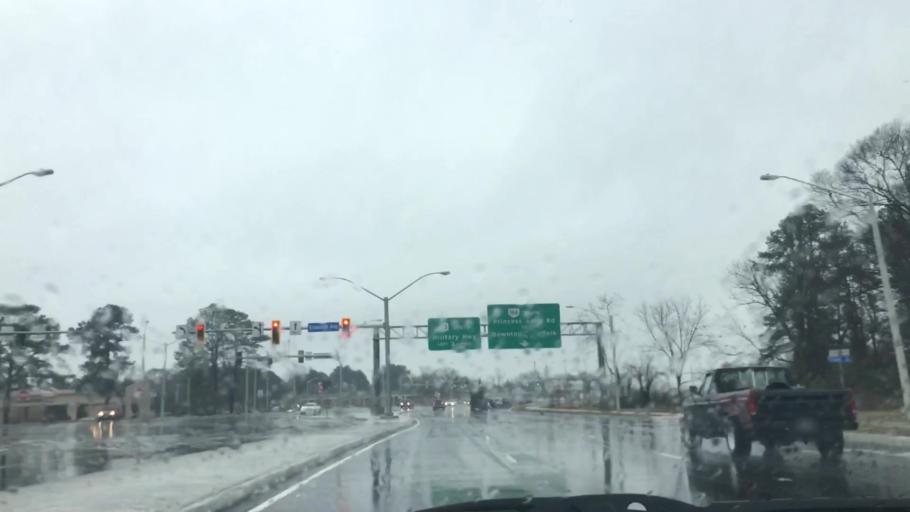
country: US
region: Virginia
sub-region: City of Norfolk
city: Norfolk
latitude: 36.8770
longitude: -76.2112
